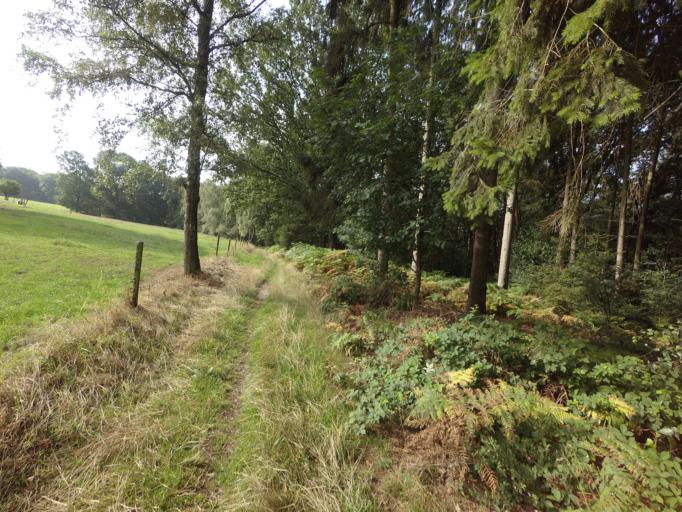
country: BE
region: Flanders
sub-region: Provincie Limburg
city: Sint-Pieters-Voeren
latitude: 50.7746
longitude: 5.8640
